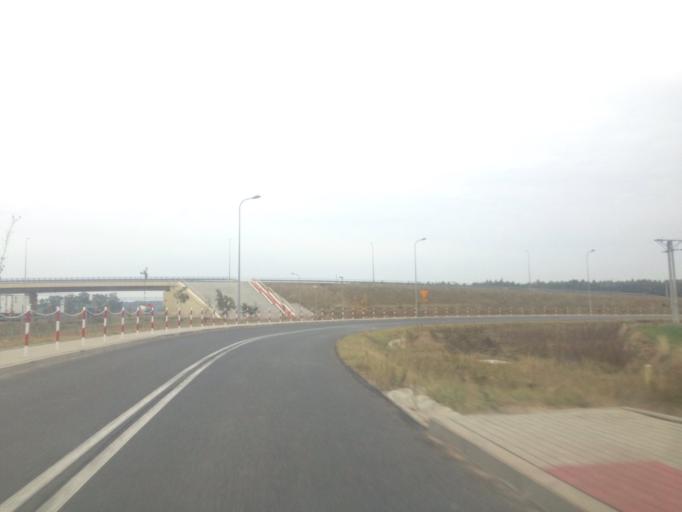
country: PL
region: Greater Poland Voivodeship
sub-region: Powiat gnieznienski
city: Lubowo
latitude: 52.4745
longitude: 17.4100
